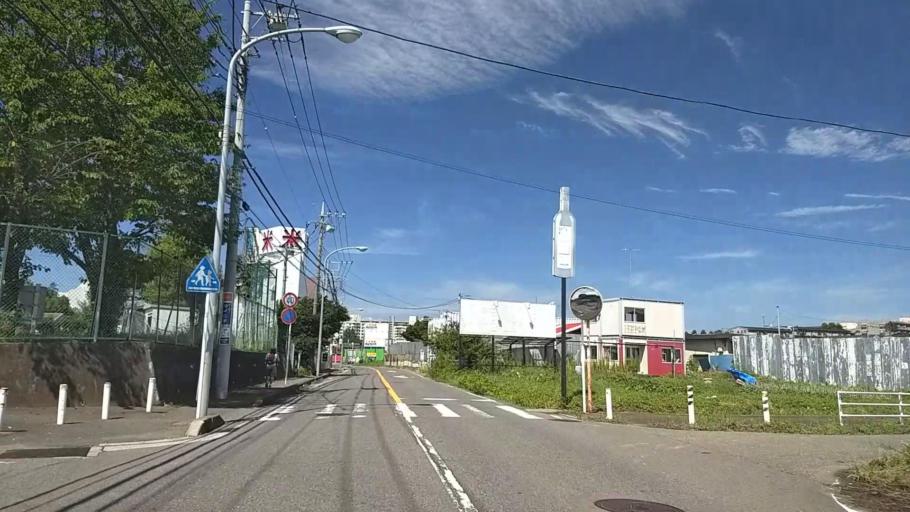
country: JP
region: Tokyo
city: Chofugaoka
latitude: 35.5572
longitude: 139.5650
